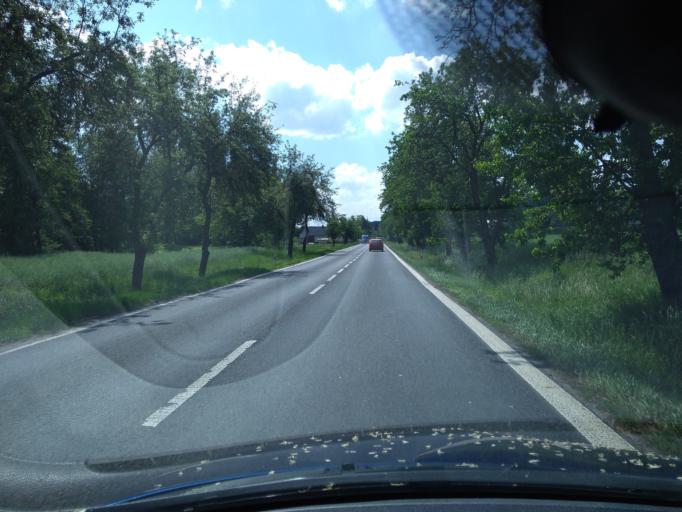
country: CZ
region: Plzensky
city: Svihov
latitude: 49.4517
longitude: 13.2888
